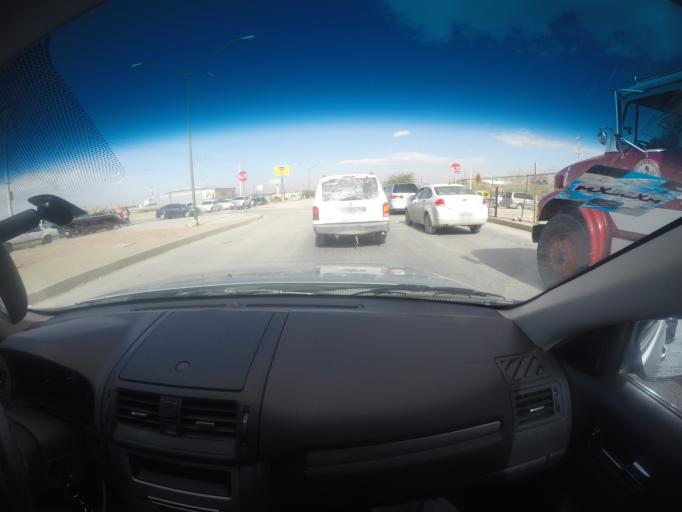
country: US
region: Texas
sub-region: El Paso County
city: Socorro Mission Number 1 Colonia
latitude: 31.6116
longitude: -106.3371
